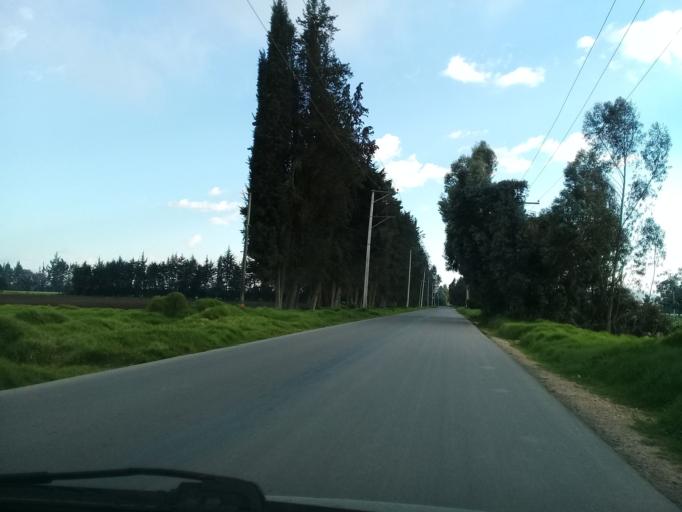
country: CO
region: Cundinamarca
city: Madrid
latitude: 4.7668
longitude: -74.2658
